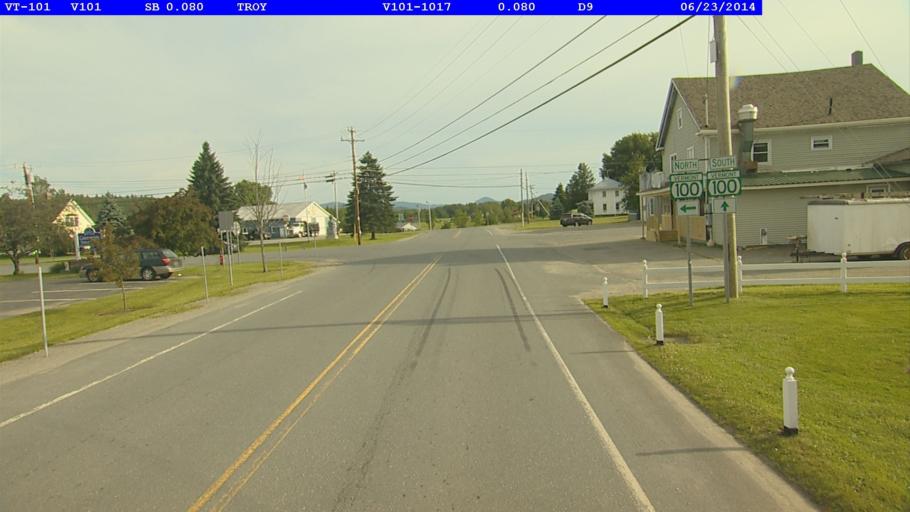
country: US
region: Vermont
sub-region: Orleans County
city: Newport
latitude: 44.9046
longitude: -72.4056
